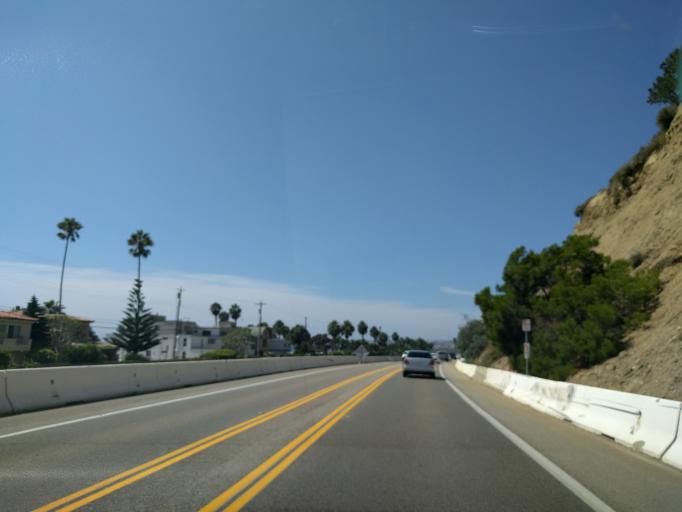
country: US
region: California
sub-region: Orange County
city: Dana Point
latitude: 33.4533
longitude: -117.6640
